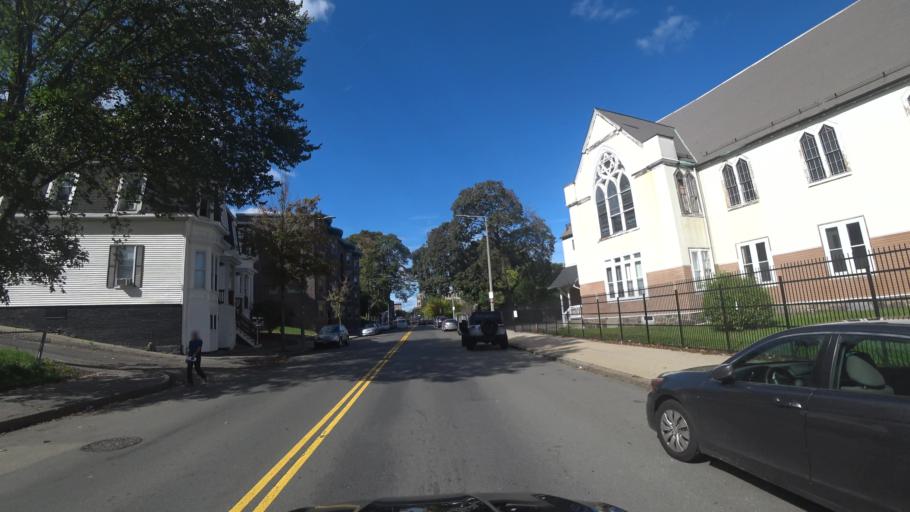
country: US
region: Massachusetts
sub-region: Suffolk County
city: South Boston
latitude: 42.3160
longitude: -71.0627
